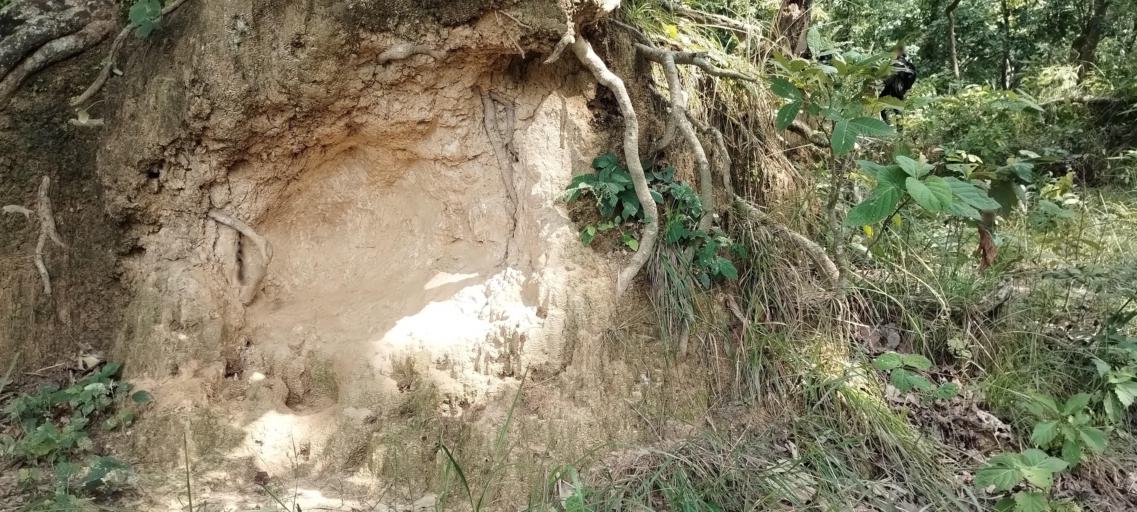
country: NP
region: Far Western
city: Tikapur
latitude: 28.4780
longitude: 81.2514
